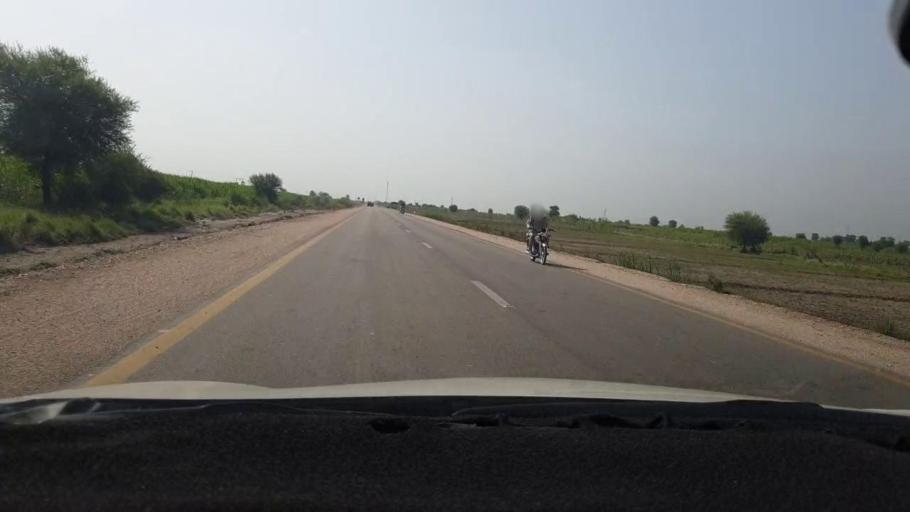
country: PK
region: Sindh
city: Jhol
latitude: 25.8413
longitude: 69.0620
